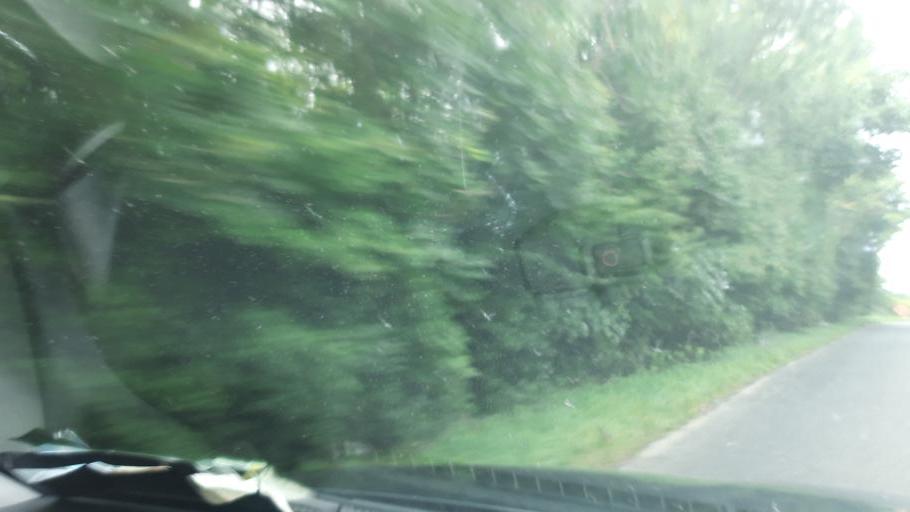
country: IE
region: Leinster
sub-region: Kilkenny
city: Callan
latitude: 52.5799
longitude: -7.3194
